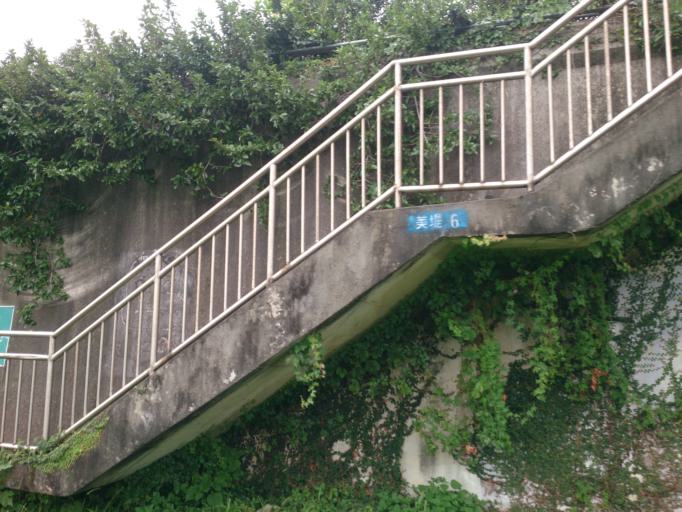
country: TW
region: Taipei
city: Taipei
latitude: 25.0768
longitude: 121.5581
